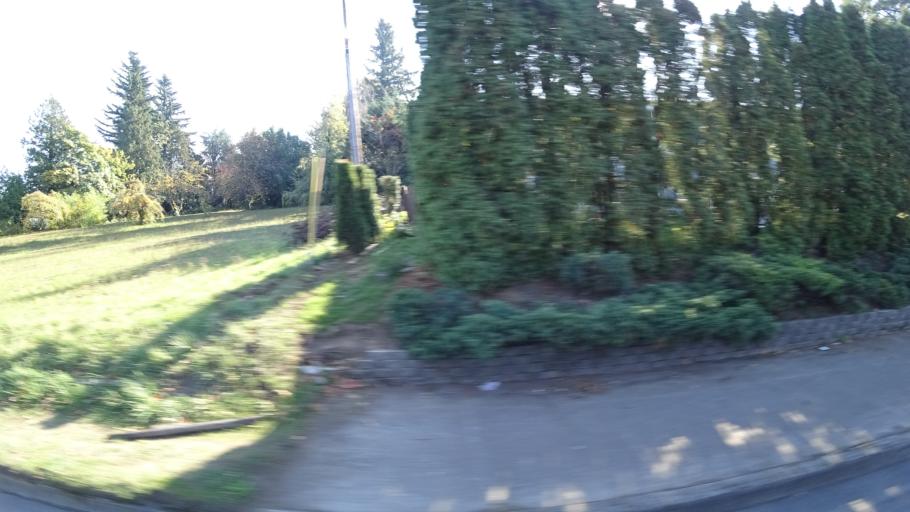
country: US
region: Oregon
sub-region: Multnomah County
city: Gresham
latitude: 45.5044
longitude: -122.4507
